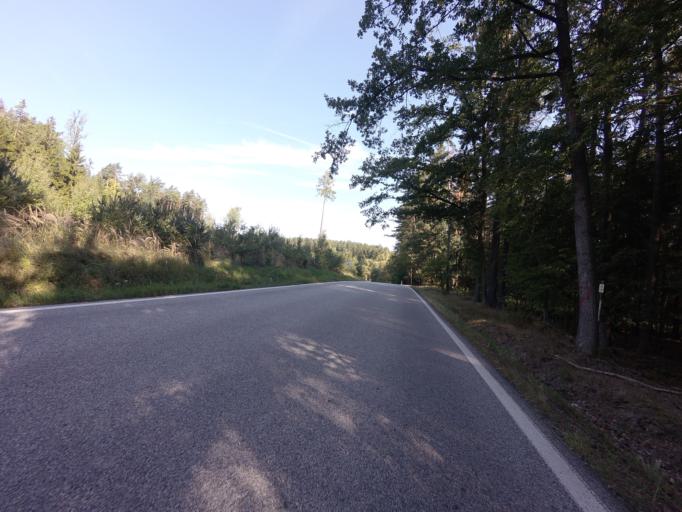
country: CZ
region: Jihocesky
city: Tyn nad Vltavou
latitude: 49.2655
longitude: 14.4114
